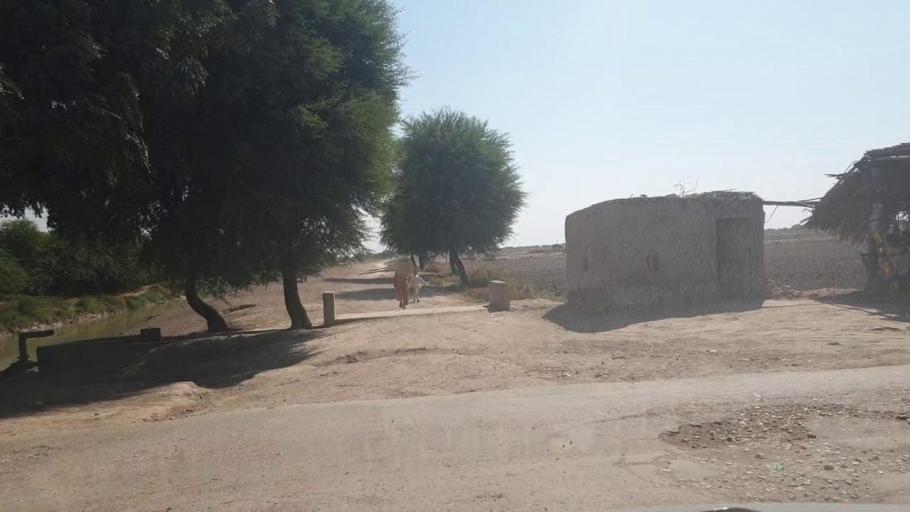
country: PK
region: Sindh
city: Digri
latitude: 24.9397
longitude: 69.1608
